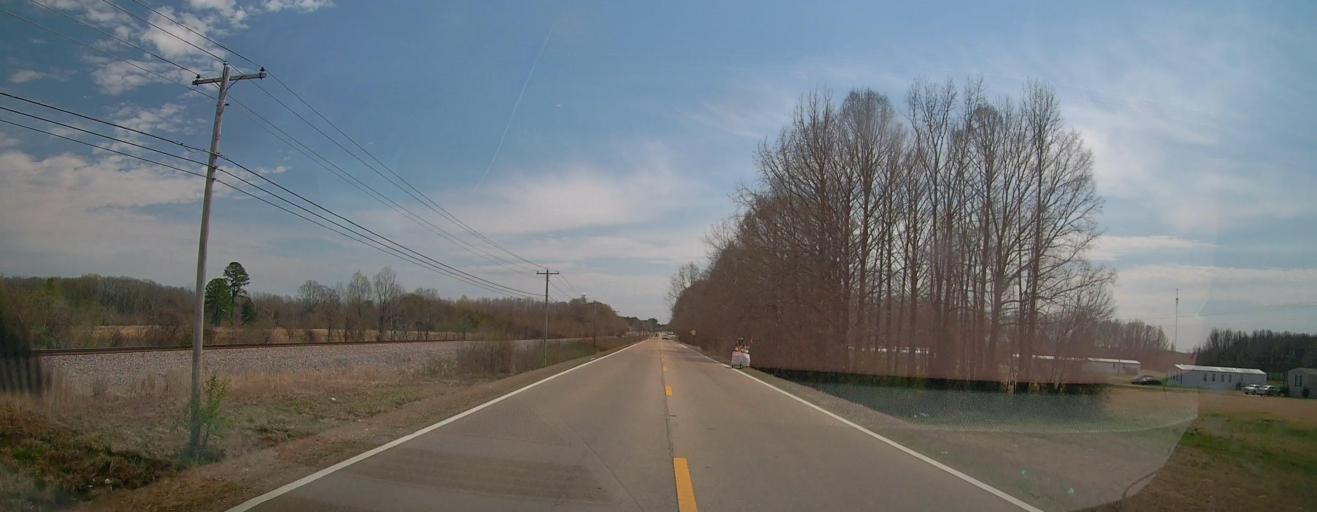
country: US
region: Mississippi
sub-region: Union County
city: New Albany
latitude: 34.5206
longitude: -89.0552
